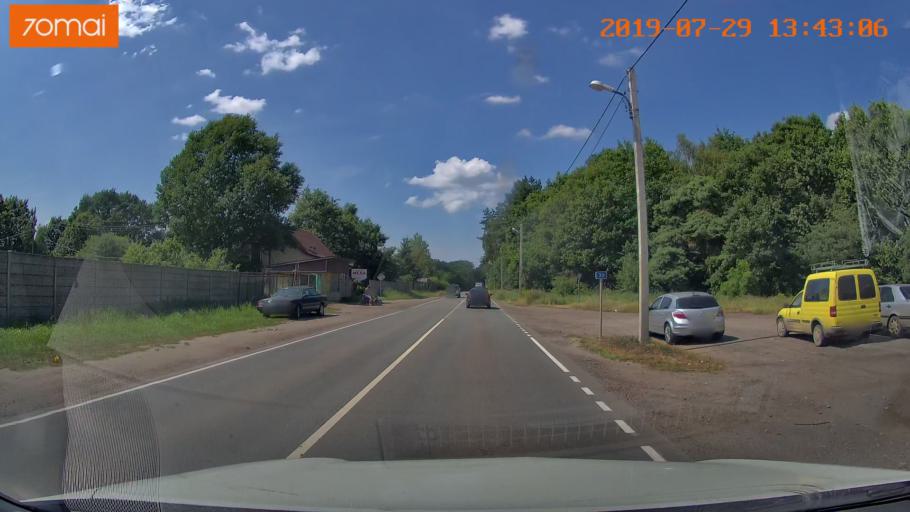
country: RU
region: Kaliningrad
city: Svetlyy
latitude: 54.7370
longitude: 20.1015
